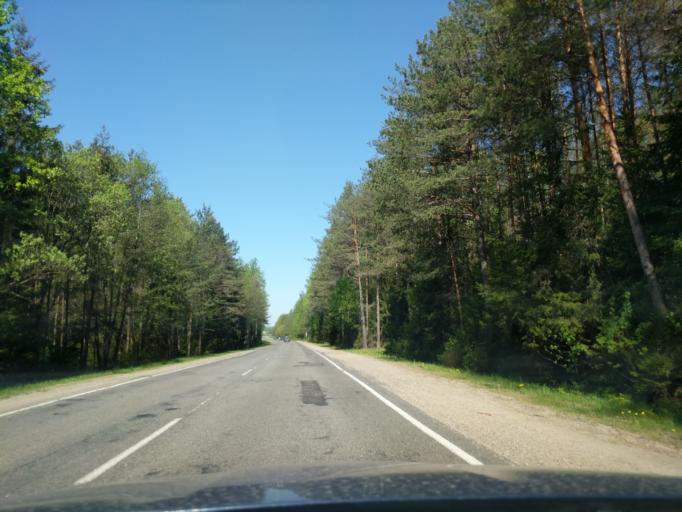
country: BY
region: Minsk
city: Il'ya
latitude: 54.4075
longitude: 27.3132
